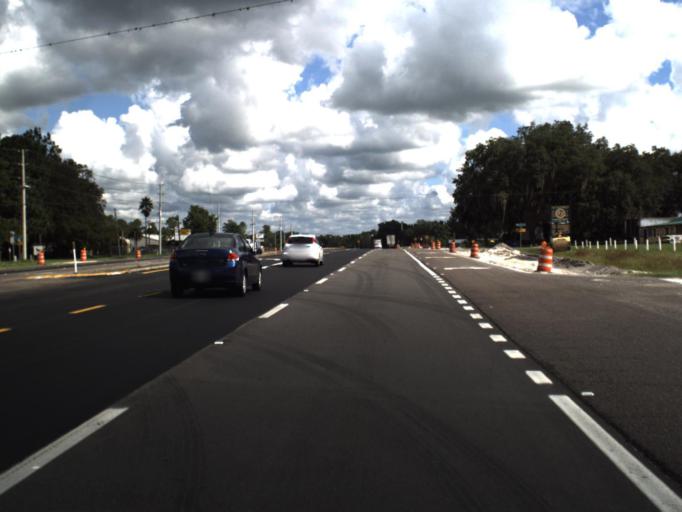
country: US
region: Florida
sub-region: Polk County
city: Gibsonia
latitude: 28.1584
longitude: -81.9736
